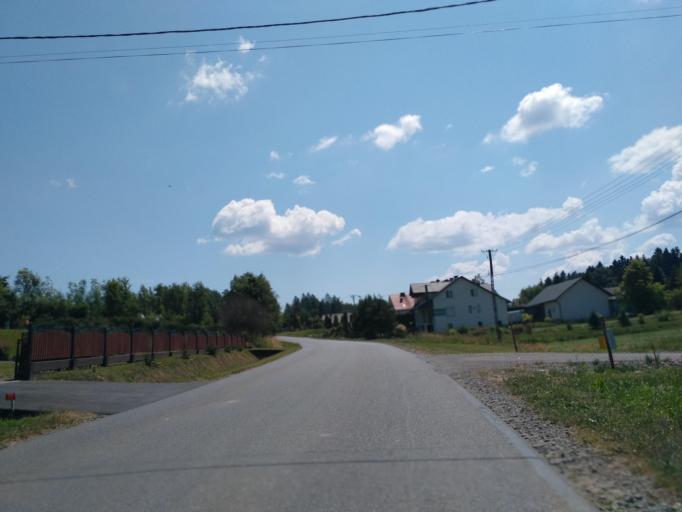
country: PL
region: Subcarpathian Voivodeship
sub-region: Powiat sanocki
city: Niebieszczany
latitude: 49.4914
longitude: 22.1786
